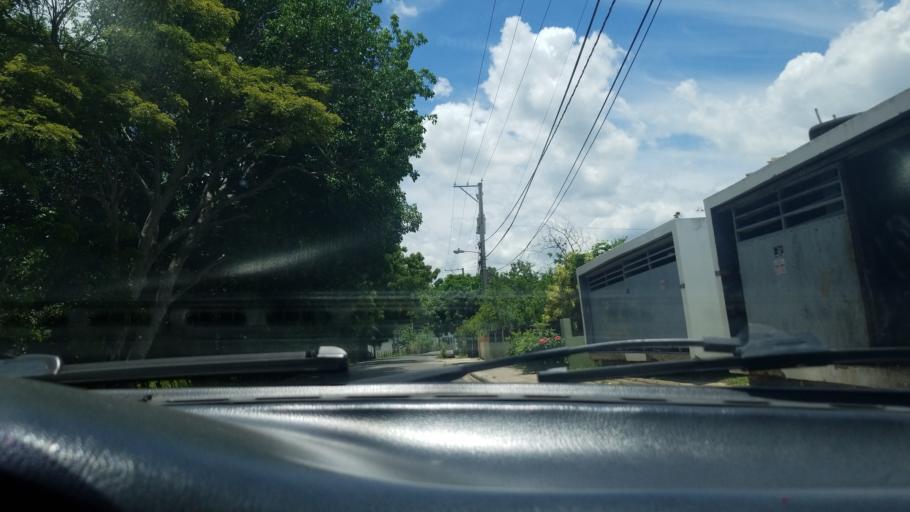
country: DO
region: Santiago
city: Santiago de los Caballeros
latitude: 19.4929
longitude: -70.6771
